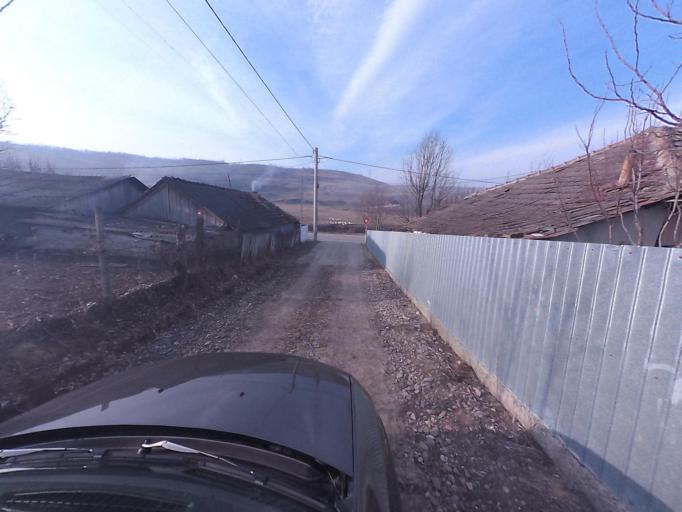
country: RO
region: Vaslui
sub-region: Comuna Solesti
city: Solesti
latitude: 46.8142
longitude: 27.7649
